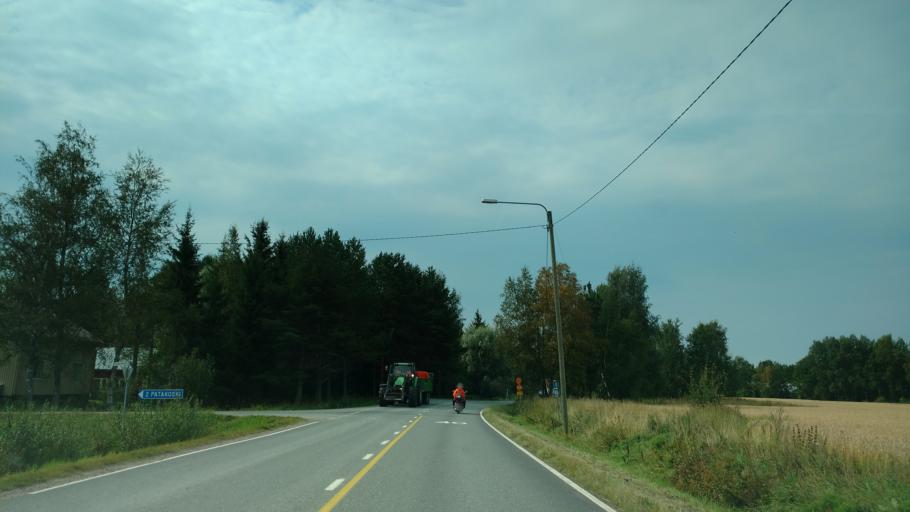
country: FI
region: Varsinais-Suomi
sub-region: Loimaa
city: Koski Tl
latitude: 60.6626
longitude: 23.1507
